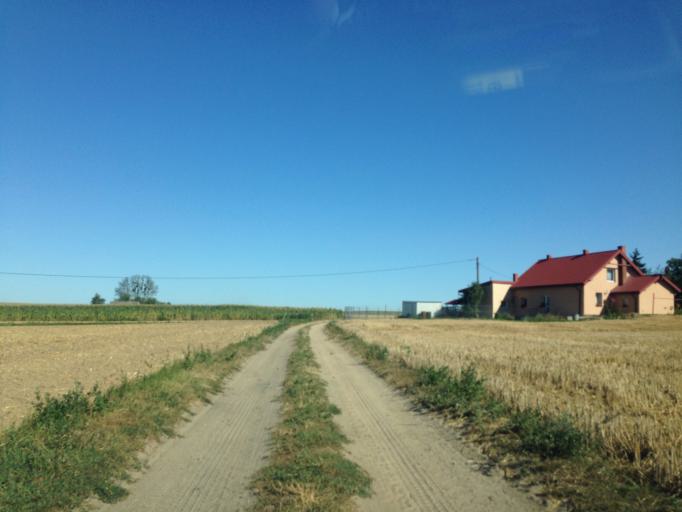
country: PL
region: Kujawsko-Pomorskie
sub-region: Powiat brodnicki
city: Brodnica
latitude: 53.2125
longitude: 19.4027
